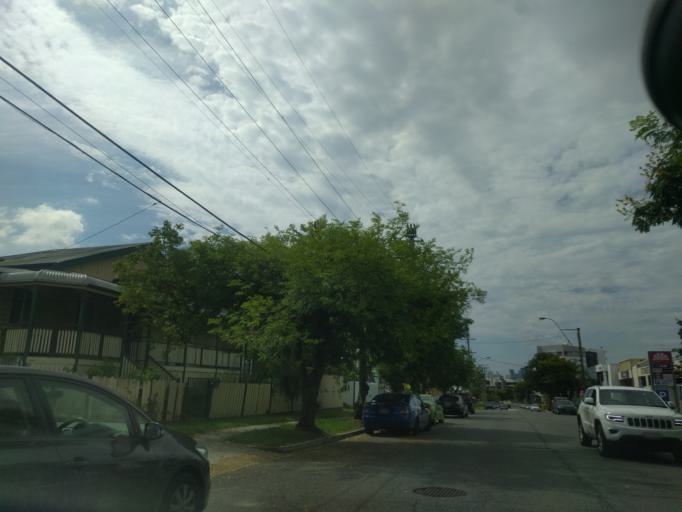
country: AU
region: Queensland
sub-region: Brisbane
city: Greenslopes
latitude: -27.5011
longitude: 153.0449
